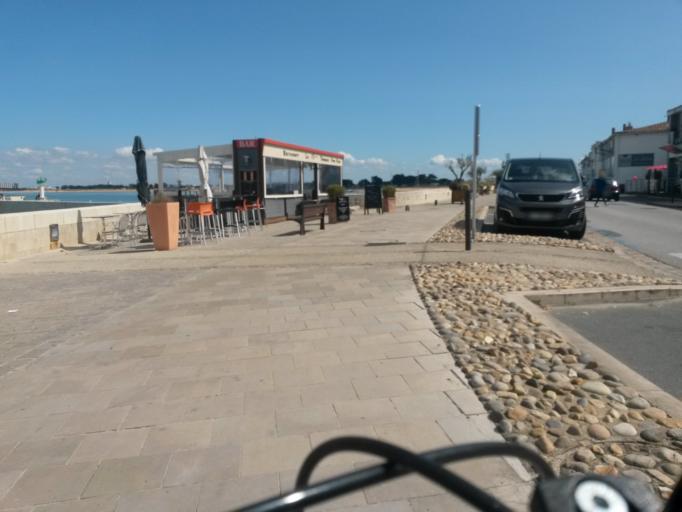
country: FR
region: Poitou-Charentes
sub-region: Departement de la Charente-Maritime
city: Rivedoux-Plage
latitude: 46.1629
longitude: -1.2788
